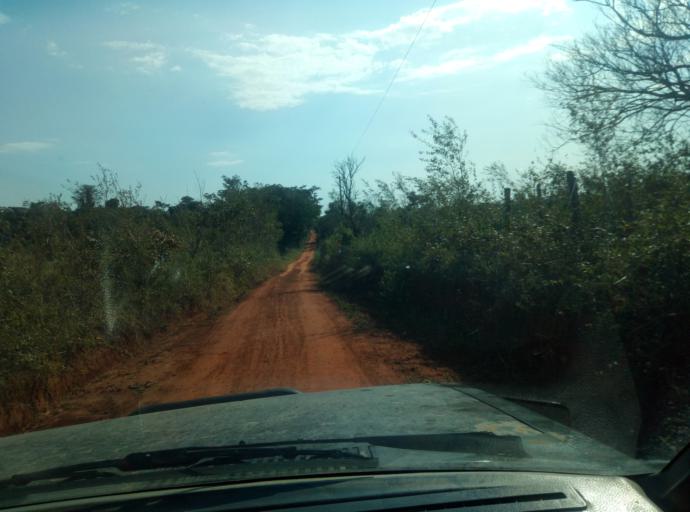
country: PY
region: Caaguazu
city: Doctor Cecilio Baez
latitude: -25.1425
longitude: -56.2536
